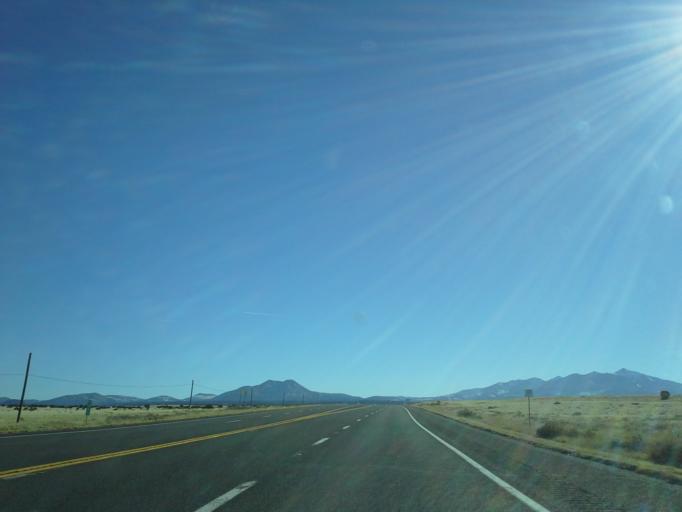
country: US
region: Arizona
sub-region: Coconino County
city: Flagstaff
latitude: 35.5784
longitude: -111.5302
